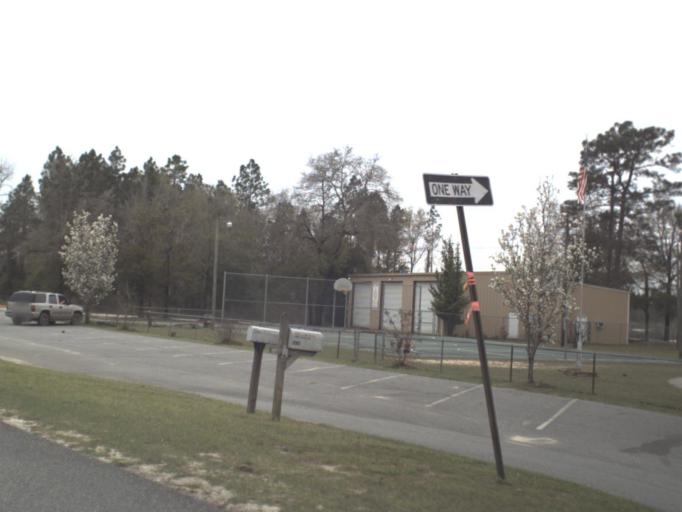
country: US
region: Florida
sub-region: Gulf County
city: Wewahitchka
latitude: 30.2658
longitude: -85.2420
